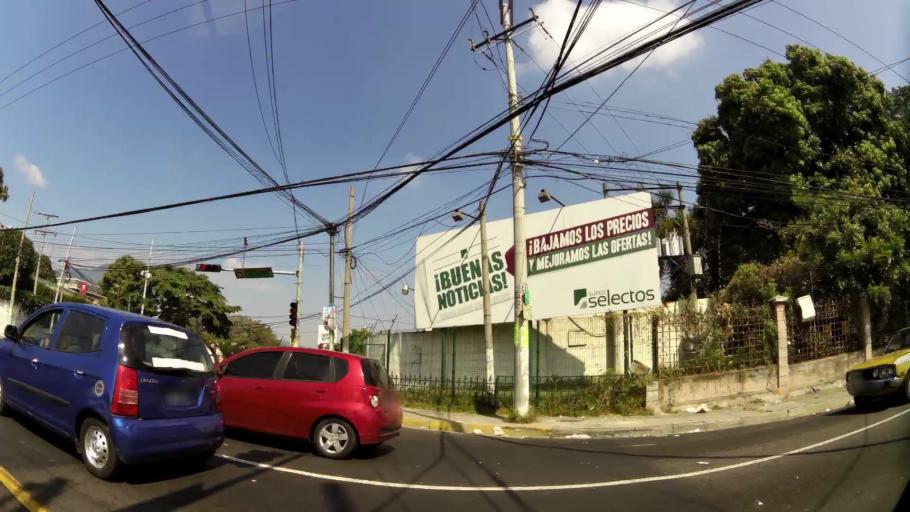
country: SV
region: San Salvador
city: San Salvador
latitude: 13.6970
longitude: -89.2209
